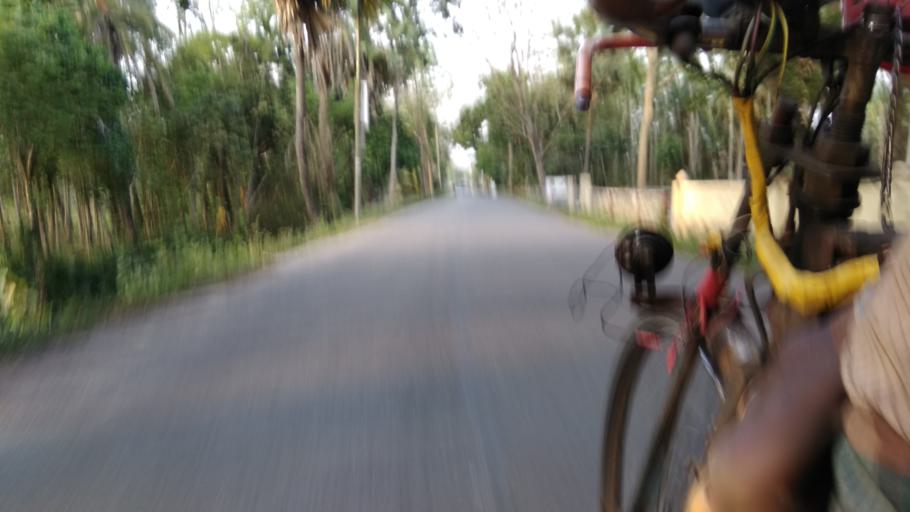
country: BD
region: Barisal
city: Mehendiganj
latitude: 22.9285
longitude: 90.4042
